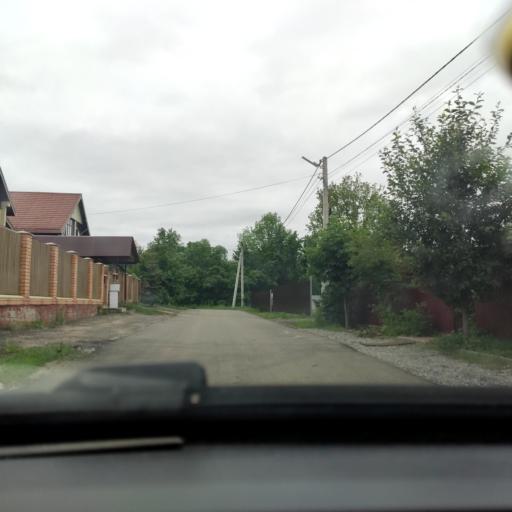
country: RU
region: Voronezj
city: Podgornoye
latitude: 51.8152
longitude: 39.1335
